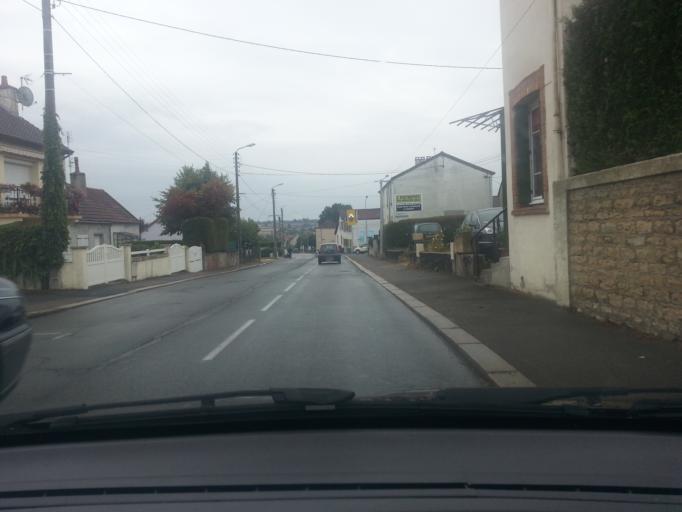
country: FR
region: Bourgogne
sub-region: Departement de Saone-et-Loire
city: Montchanin
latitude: 46.7433
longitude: 4.4721
